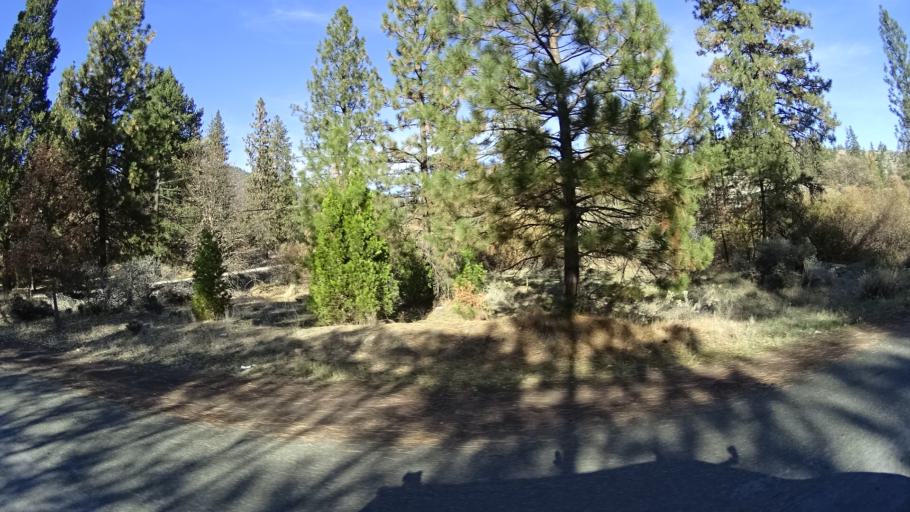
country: US
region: California
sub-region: Siskiyou County
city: Yreka
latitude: 41.7196
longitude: -122.6853
